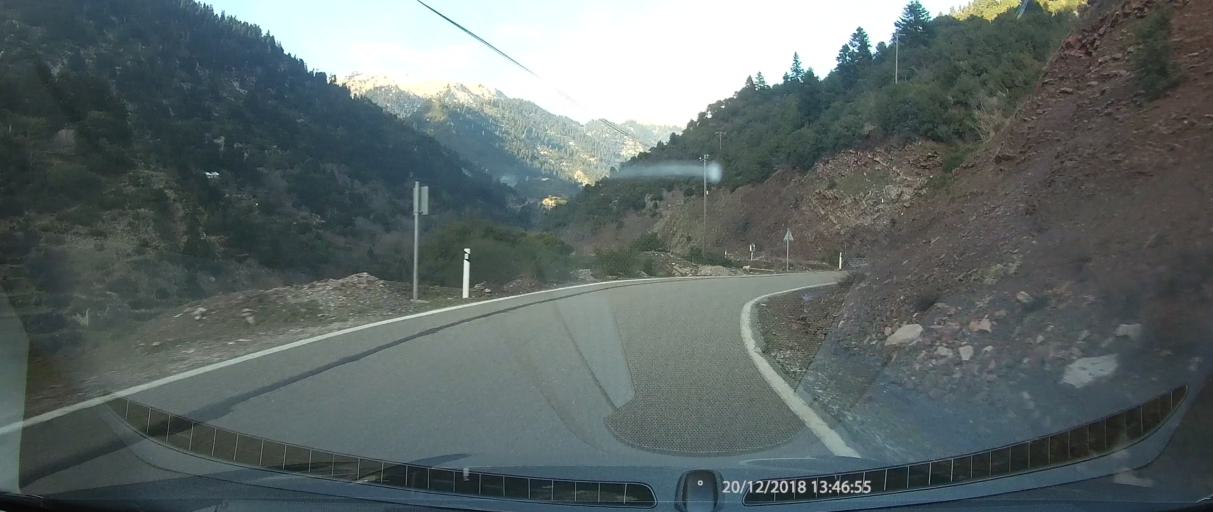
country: GR
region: West Greece
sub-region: Nomos Aitolias kai Akarnanias
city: Thermo
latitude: 38.6773
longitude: 21.6173
